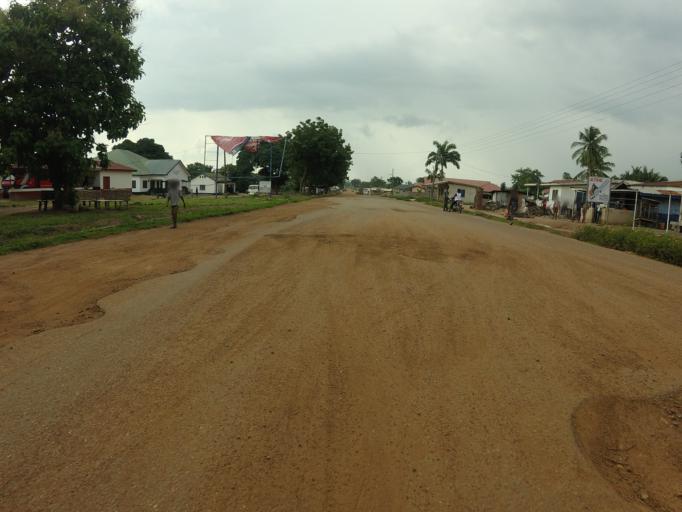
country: GH
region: Volta
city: Kpandu
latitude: 7.0004
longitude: 0.4369
